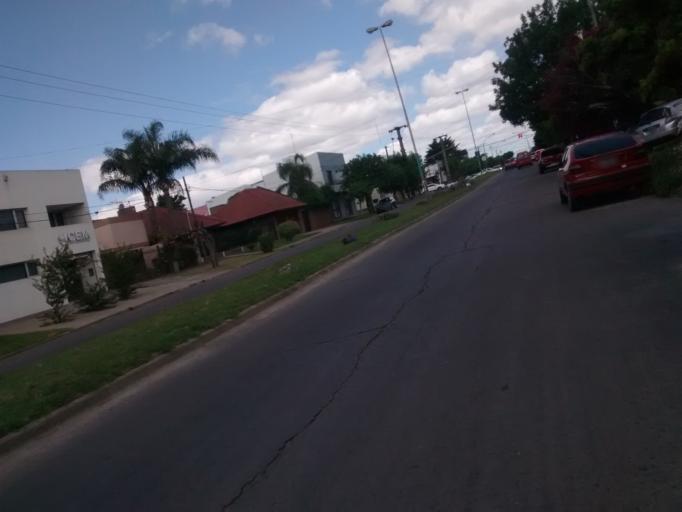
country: AR
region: Buenos Aires
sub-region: Partido de La Plata
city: La Plata
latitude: -34.9384
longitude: -57.9876
